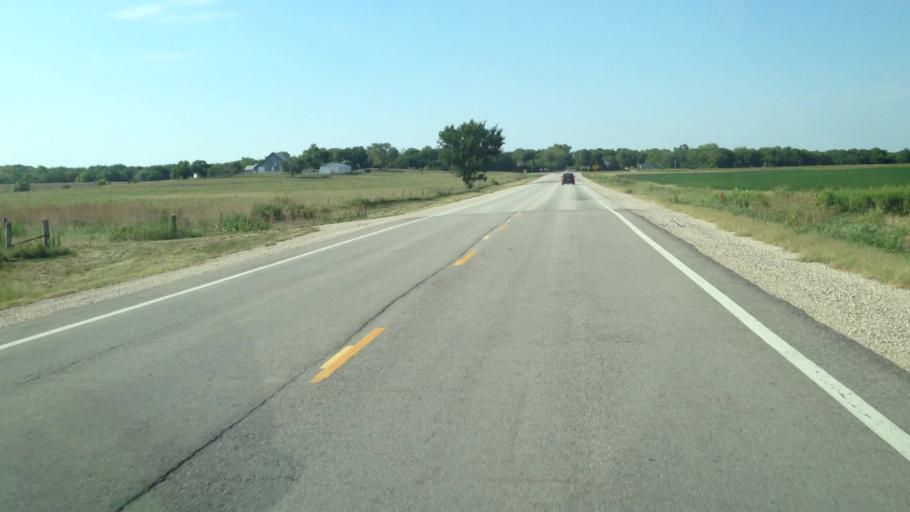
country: US
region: Kansas
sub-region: Anderson County
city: Garnett
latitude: 38.0762
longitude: -95.1694
